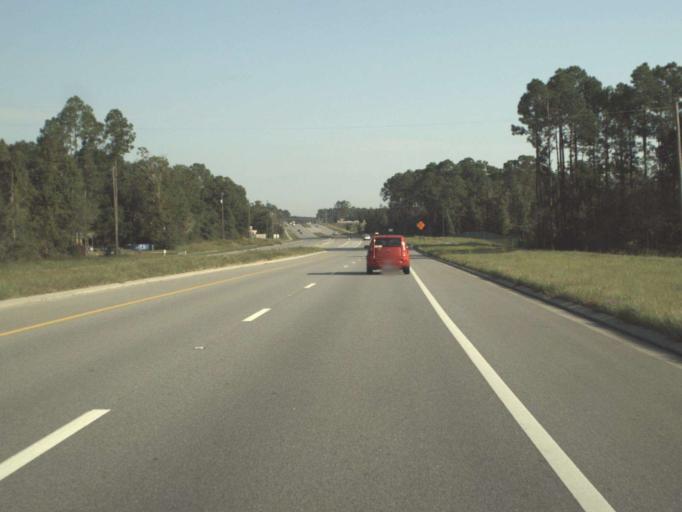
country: US
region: Florida
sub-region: Bay County
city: Laguna Beach
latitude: 30.4328
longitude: -85.8742
